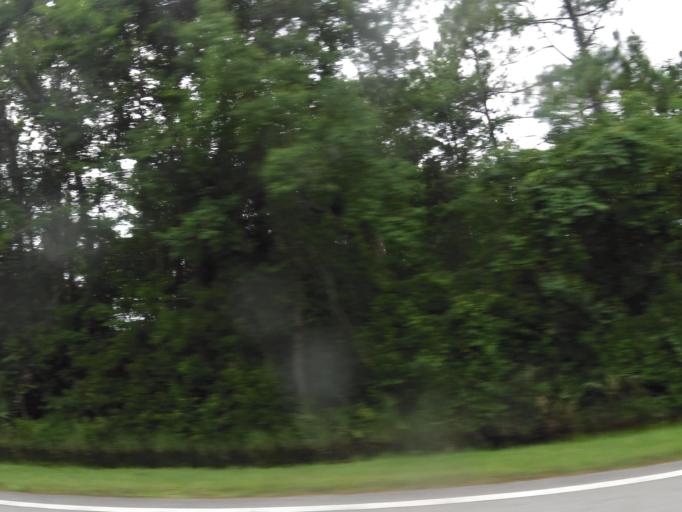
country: US
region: Florida
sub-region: Saint Johns County
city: Saint Augustine
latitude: 29.8754
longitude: -81.3656
